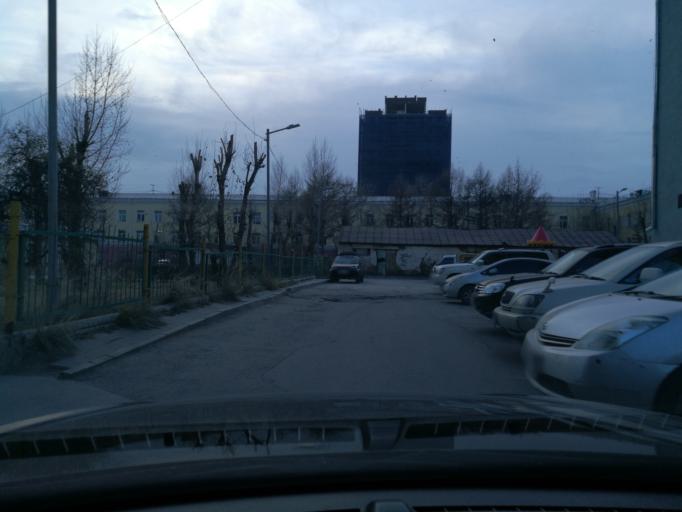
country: MN
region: Ulaanbaatar
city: Ulaanbaatar
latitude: 47.9243
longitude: 106.9198
